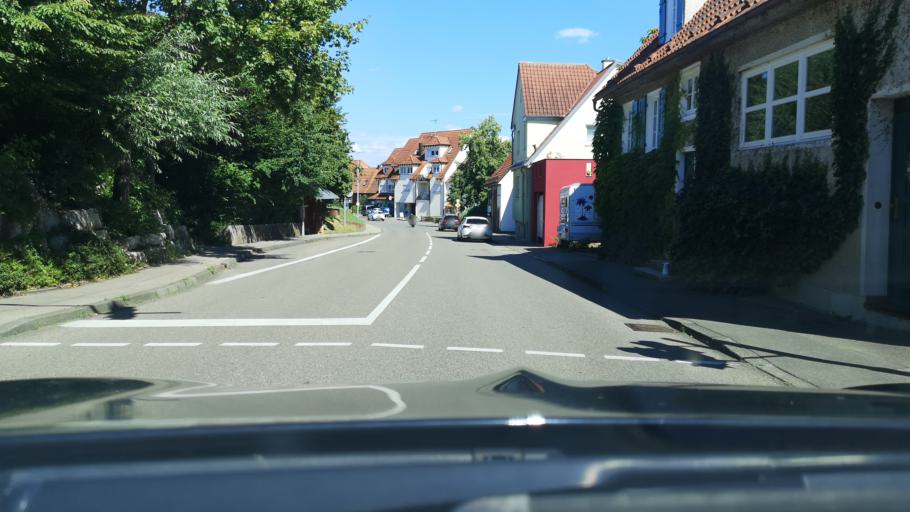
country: DE
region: Baden-Wuerttemberg
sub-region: Regierungsbezirk Stuttgart
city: Altenriet
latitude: 48.5902
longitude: 9.2173
